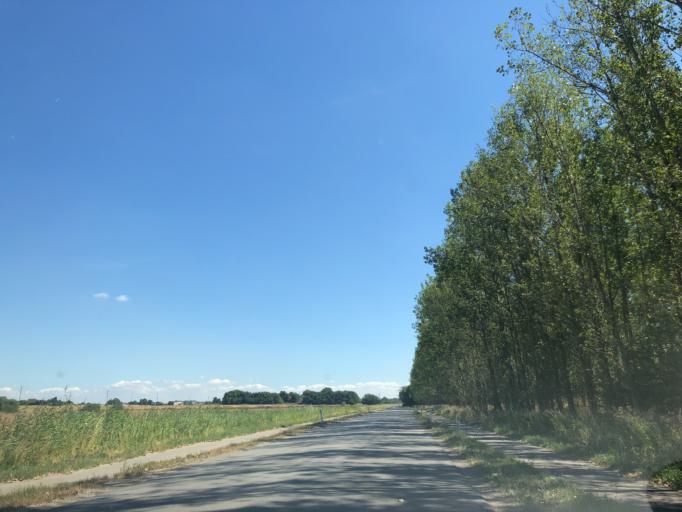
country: DK
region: Zealand
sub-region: Slagelse Kommune
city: Forlev
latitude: 55.3744
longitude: 11.2313
